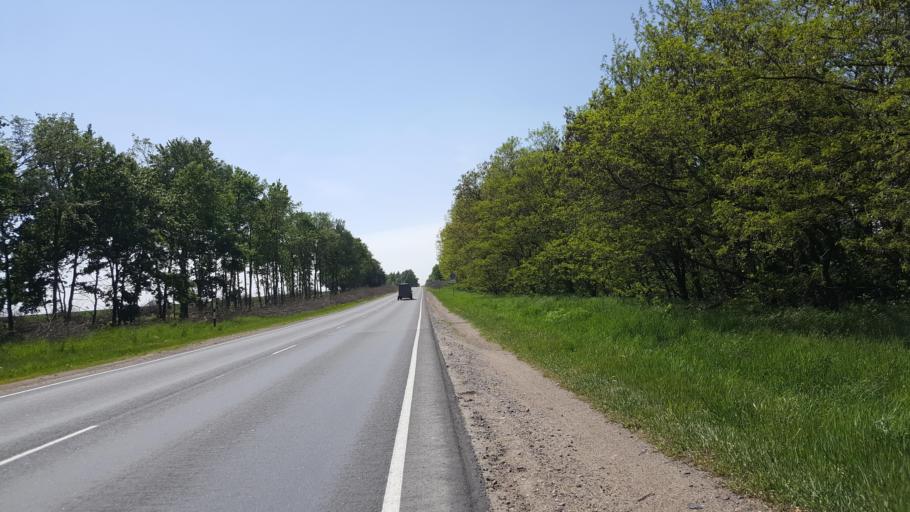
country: BY
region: Brest
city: Charnawchytsy
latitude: 52.2434
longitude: 23.7482
